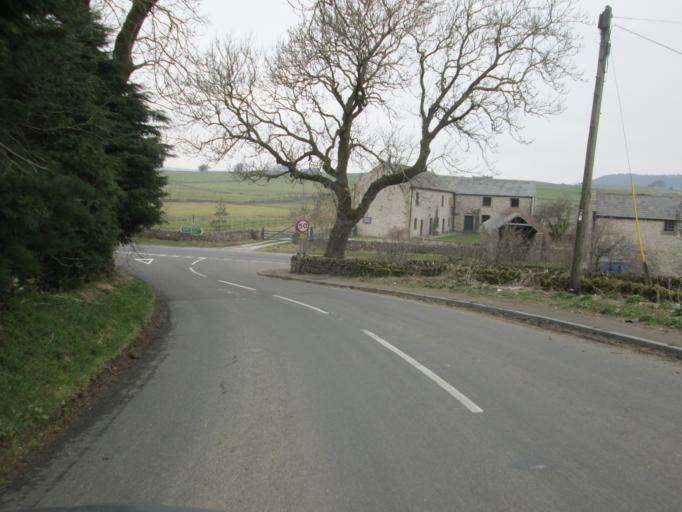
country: GB
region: England
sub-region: Derbyshire
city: Tideswell
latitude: 53.2767
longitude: -1.7304
